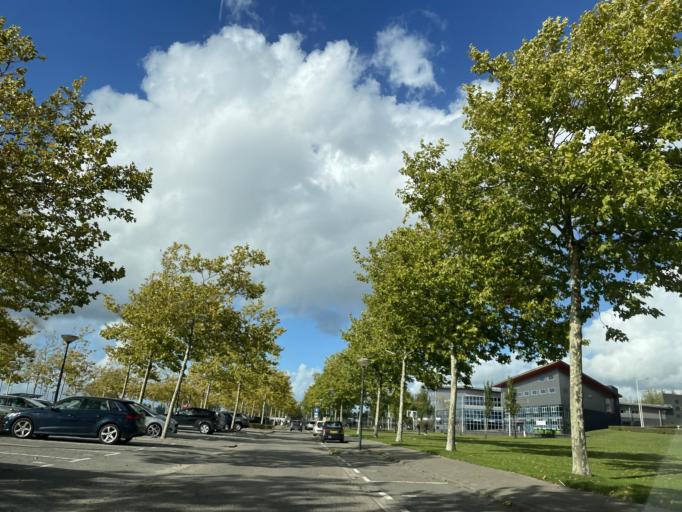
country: NL
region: North Brabant
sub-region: Gemeente Bergen op Zoom
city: Bergen op Zoom
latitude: 51.4848
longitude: 4.2785
